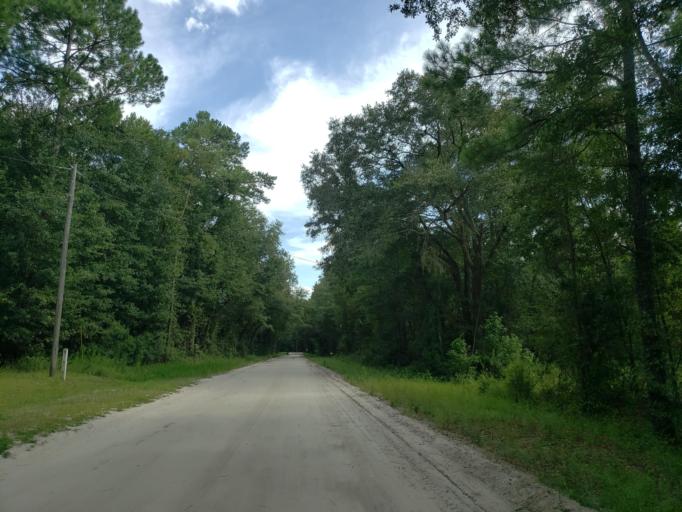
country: US
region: Florida
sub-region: Hamilton County
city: Jasper
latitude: 30.5536
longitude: -83.0869
